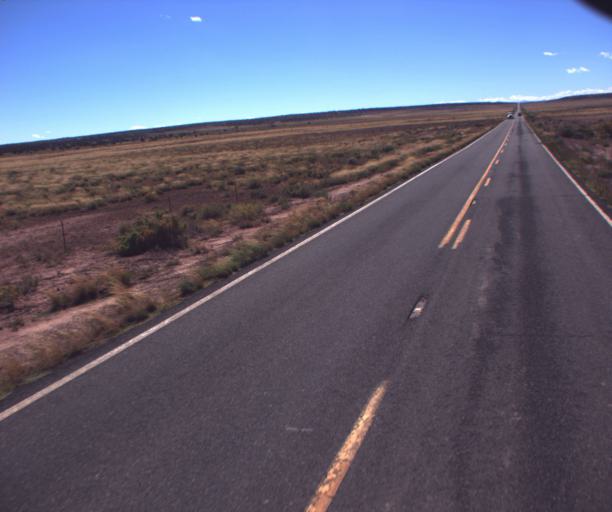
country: US
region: Arizona
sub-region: Apache County
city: Saint Johns
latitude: 34.6961
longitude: -109.2737
